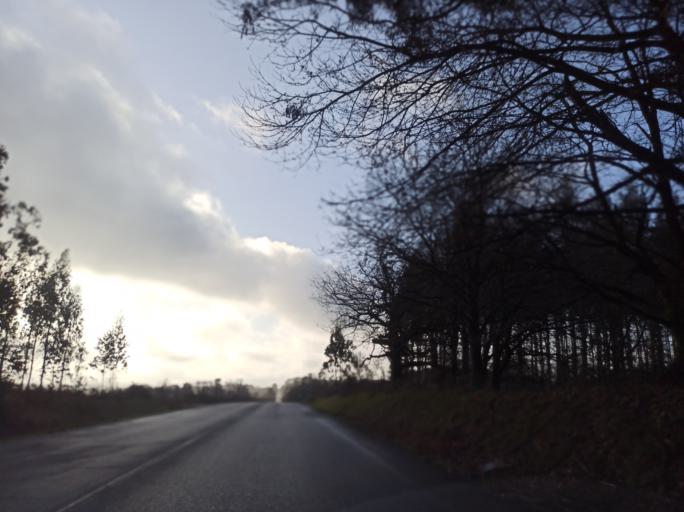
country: ES
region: Galicia
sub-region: Provincia da Coruna
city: Curtis
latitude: 43.0996
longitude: -8.0208
